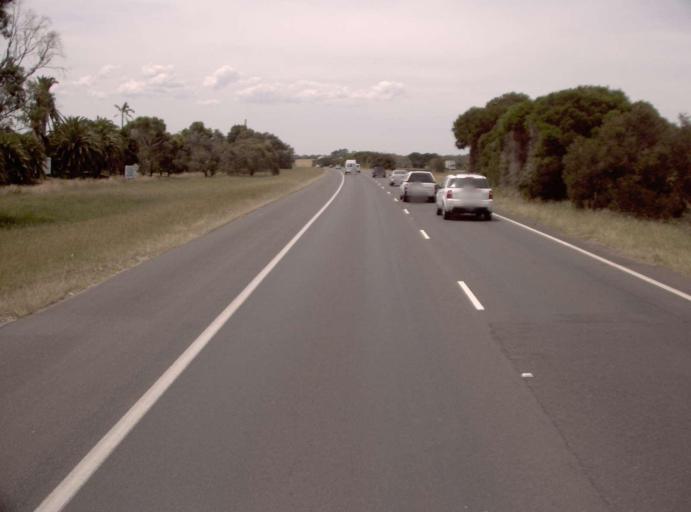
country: AU
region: Victoria
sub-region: Mornington Peninsula
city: Safety Beach
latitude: -38.3230
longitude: 145.0029
